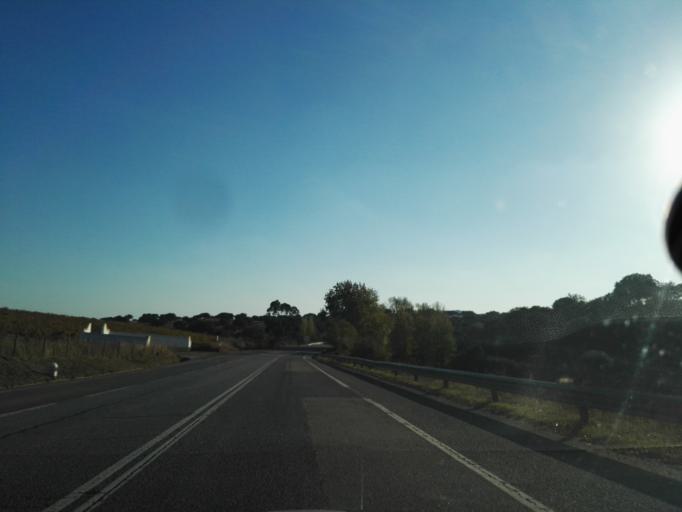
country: PT
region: Evora
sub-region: Vila Vicosa
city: Vila Vicosa
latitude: 38.8338
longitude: -7.4036
